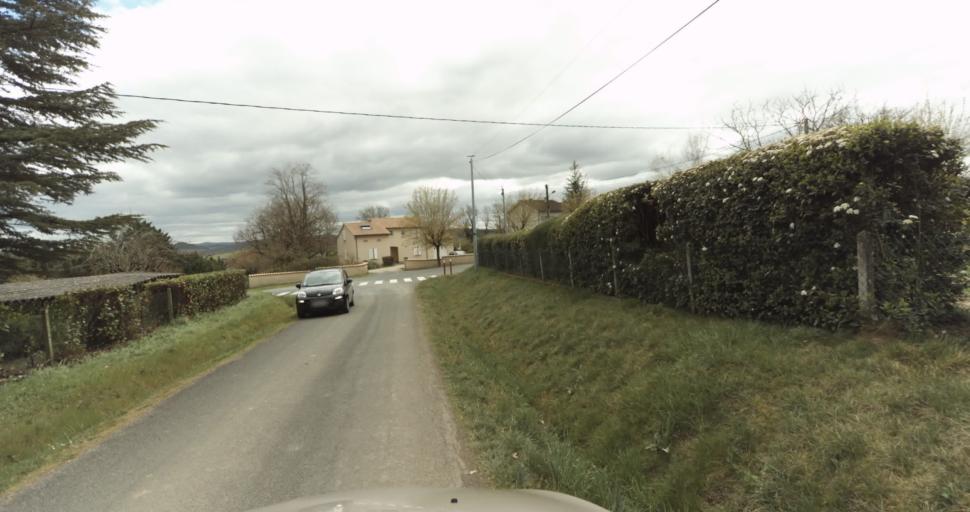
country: FR
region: Midi-Pyrenees
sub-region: Departement du Tarn
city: Puygouzon
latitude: 43.8953
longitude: 2.1777
